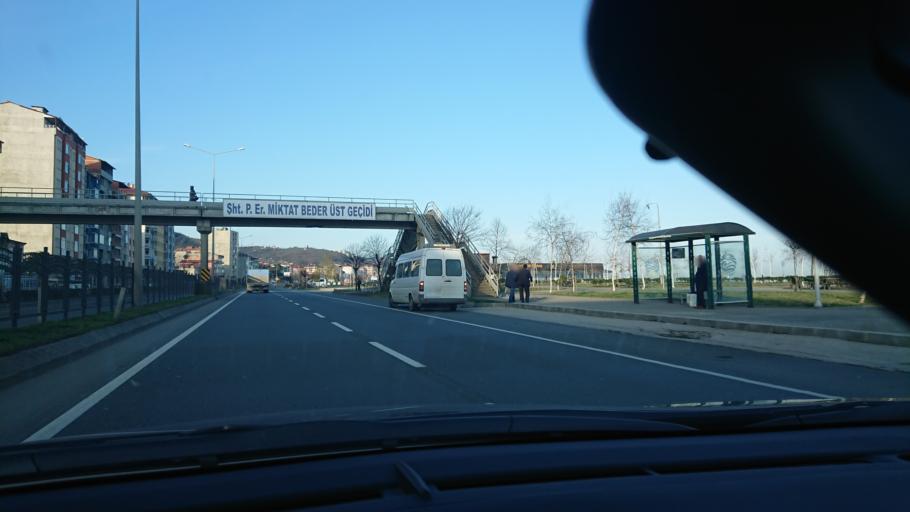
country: TR
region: Trabzon
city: Arsin
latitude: 40.9546
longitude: 39.9346
